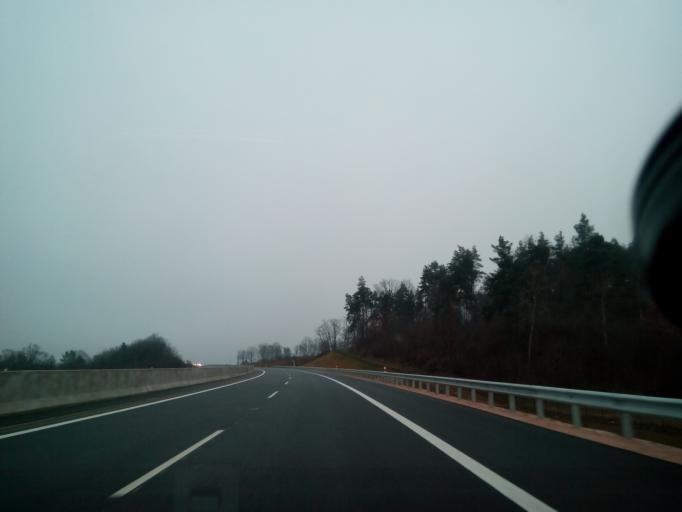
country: SK
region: Presovsky
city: Sabinov
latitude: 49.0113
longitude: 21.0437
